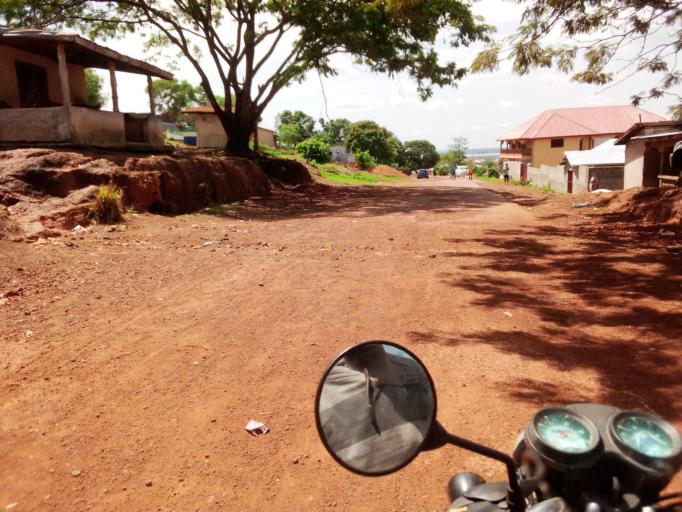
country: SL
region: Western Area
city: Waterloo
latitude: 8.3500
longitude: -13.0791
